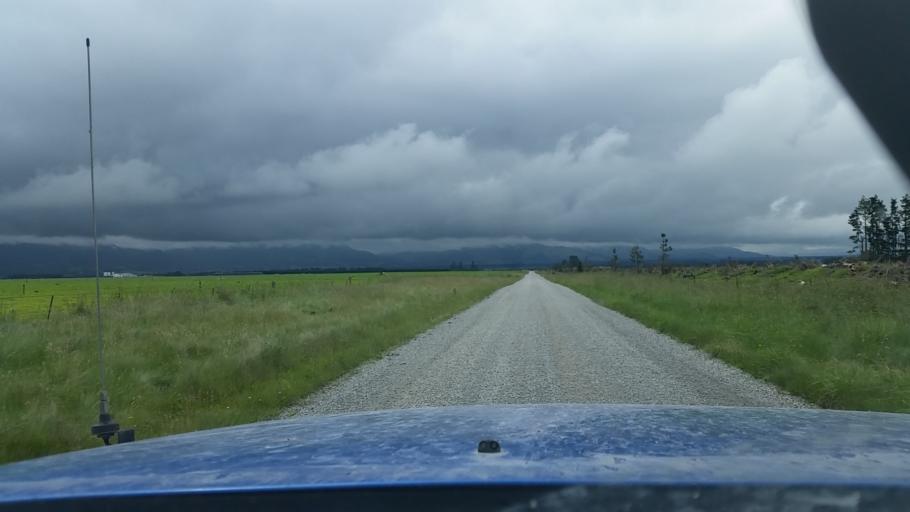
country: NZ
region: Canterbury
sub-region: Ashburton District
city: Methven
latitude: -43.7144
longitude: 171.4583
